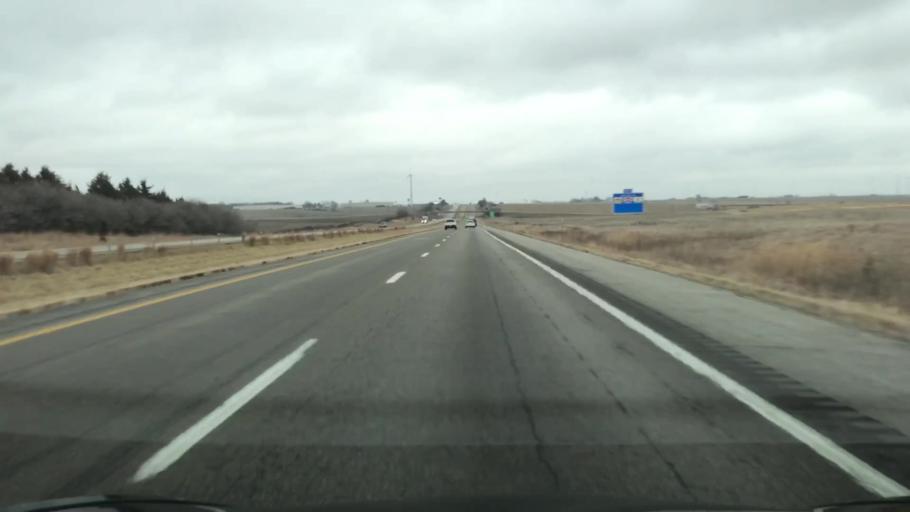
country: US
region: Iowa
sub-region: Guthrie County
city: Stuart
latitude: 41.4929
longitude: -94.3493
